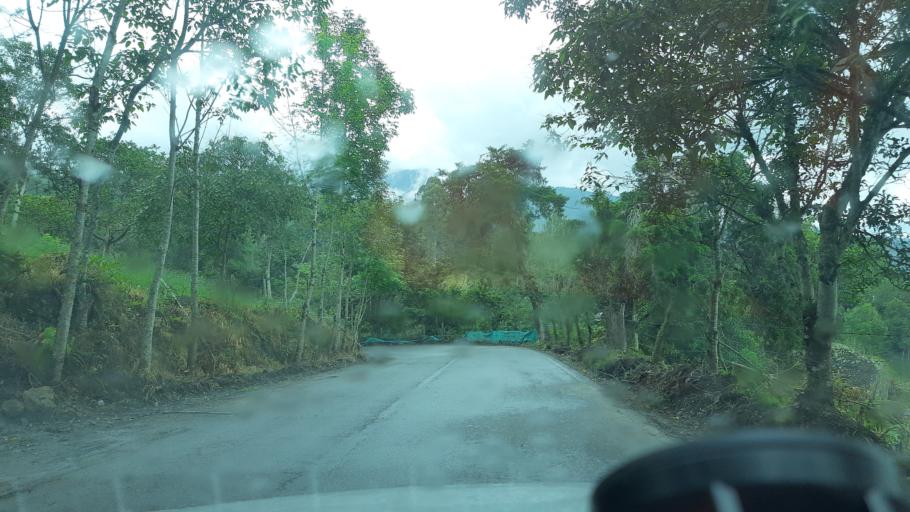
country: CO
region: Boyaca
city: Chinavita
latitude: 5.1519
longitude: -73.3636
